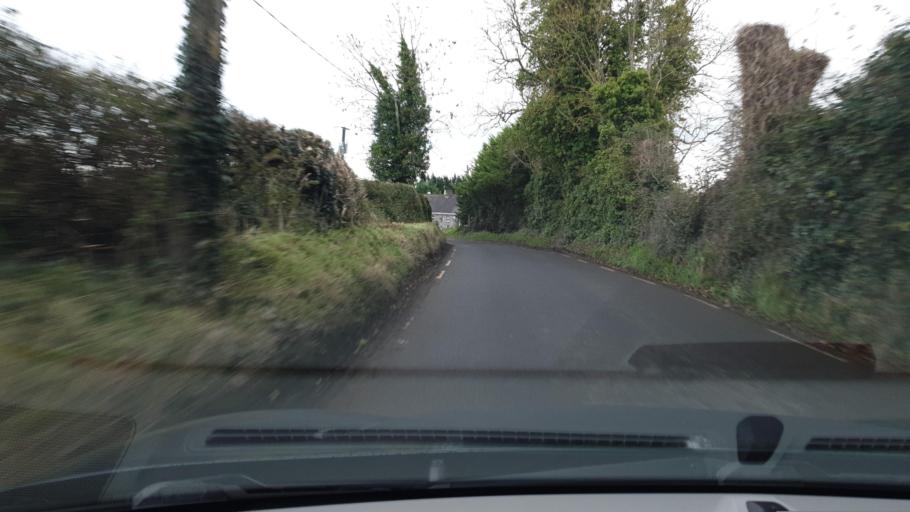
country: IE
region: Leinster
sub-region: An Mhi
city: Ashbourne
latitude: 53.5338
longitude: -6.3974
